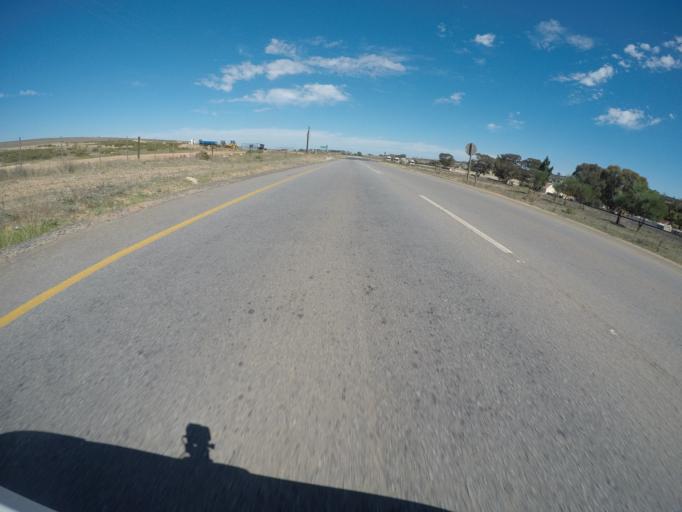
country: ZA
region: Western Cape
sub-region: West Coast District Municipality
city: Malmesbury
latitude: -33.4908
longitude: 18.6843
